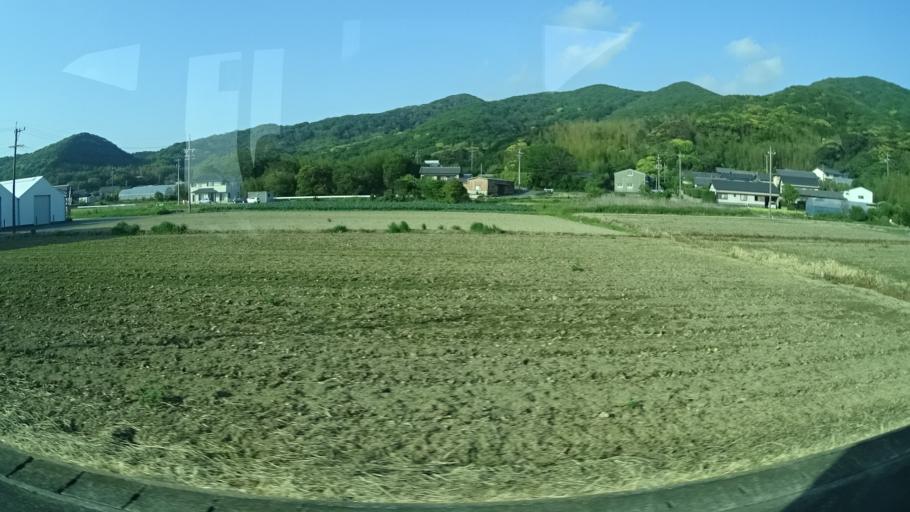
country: JP
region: Aichi
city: Tahara
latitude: 34.6526
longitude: 137.2165
